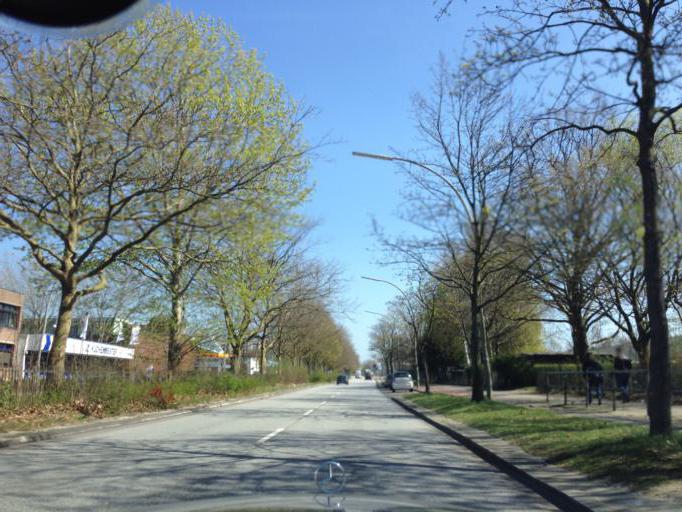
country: DE
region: Hamburg
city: Barmbek-Nord
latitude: 53.6083
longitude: 10.0491
